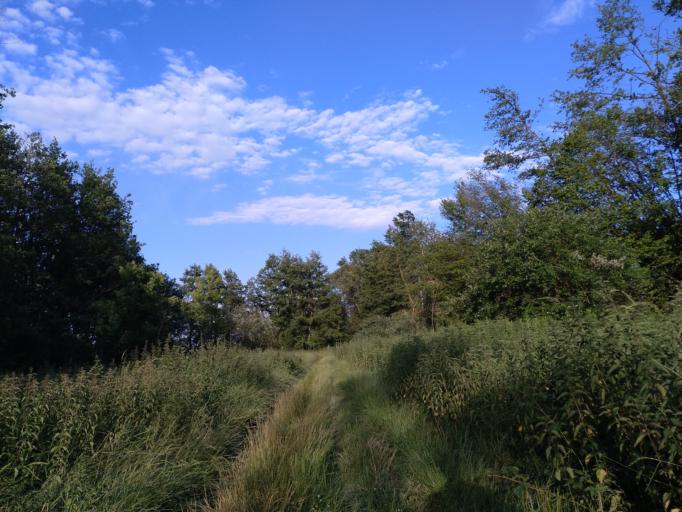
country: FR
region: Rhone-Alpes
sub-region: Departement du Rhone
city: Simandres
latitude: 45.6342
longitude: 4.8880
